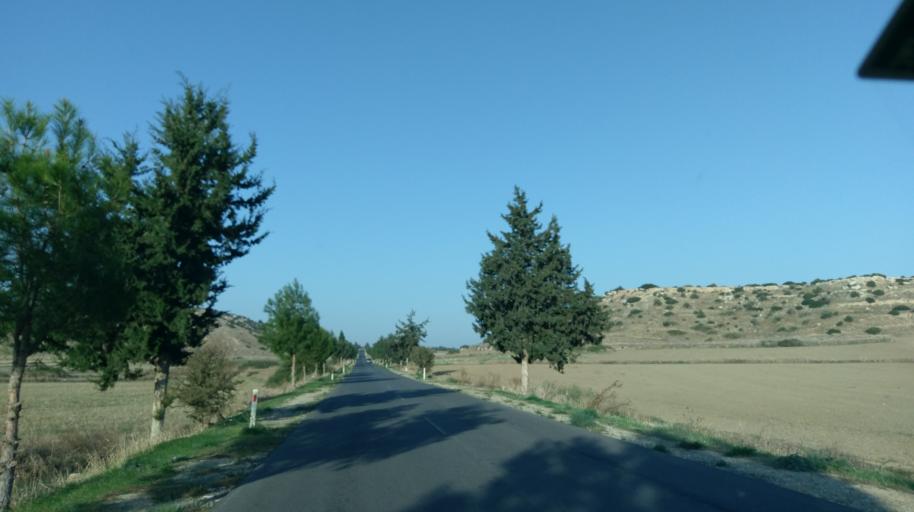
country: CY
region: Ammochostos
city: Leonarisso
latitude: 35.3882
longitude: 34.0453
